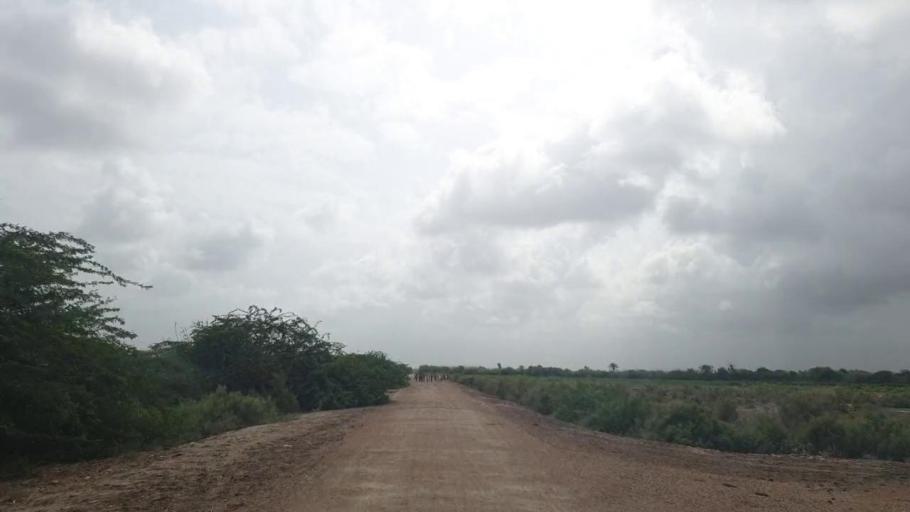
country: PK
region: Sindh
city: Tando Bago
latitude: 24.8333
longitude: 69.1032
